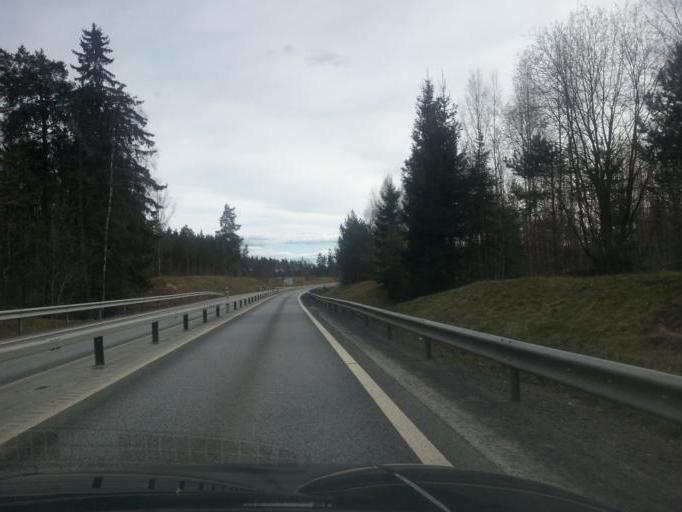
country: SE
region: Joenkoeping
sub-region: Jonkopings Kommun
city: Bankeryd
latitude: 57.8800
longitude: 14.1040
